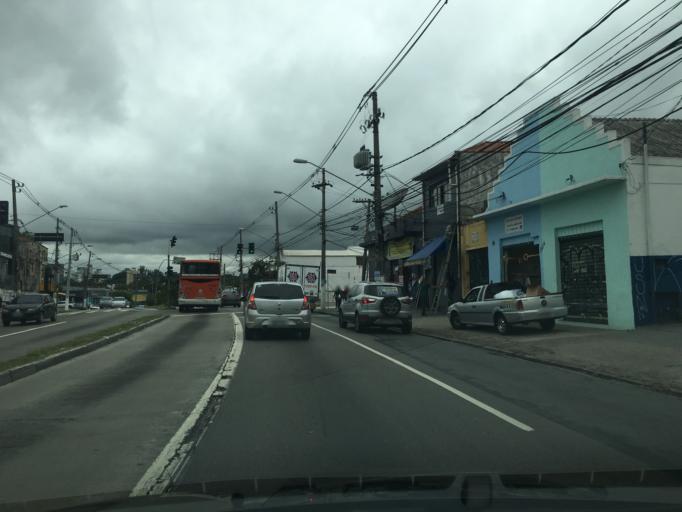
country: BR
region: Sao Paulo
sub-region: Taboao Da Serra
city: Taboao da Serra
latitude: -23.5847
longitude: -46.7181
